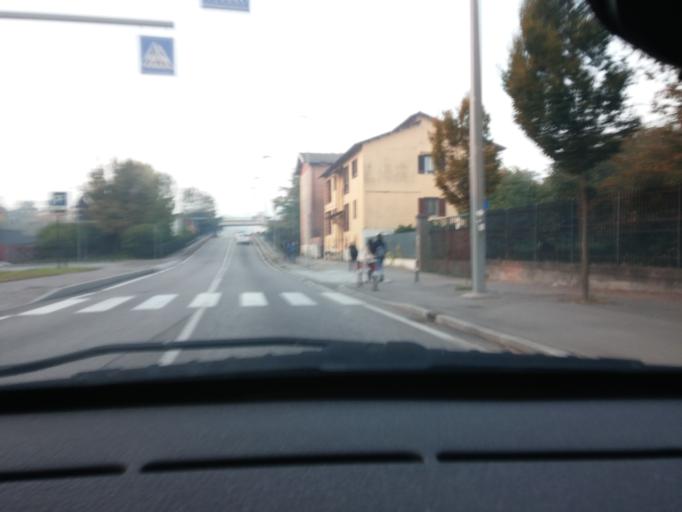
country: IT
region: Emilia-Romagna
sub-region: Provincia di Ferrara
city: Ferrara
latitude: 44.8380
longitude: 11.6006
